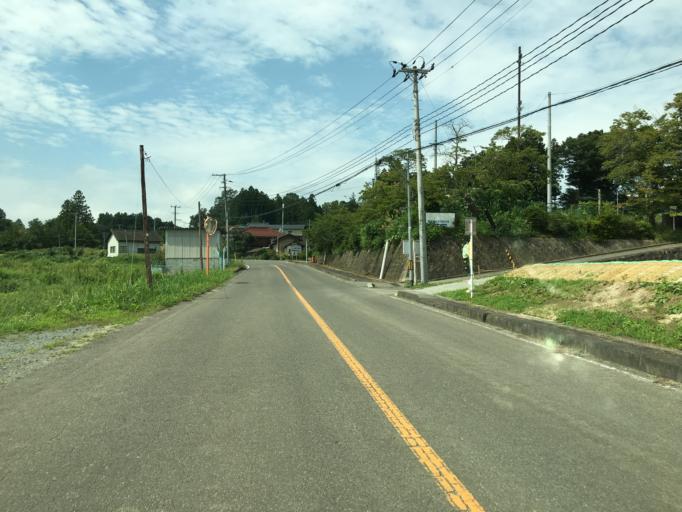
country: JP
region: Fukushima
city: Fukushima-shi
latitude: 37.6582
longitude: 140.5230
